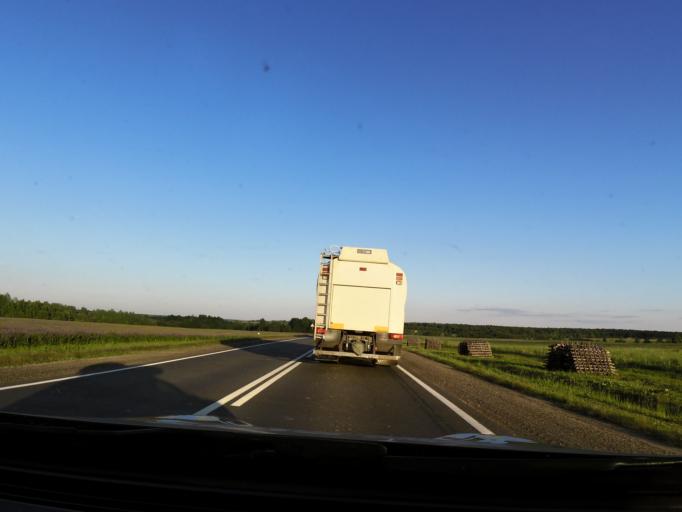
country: RU
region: Vologda
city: Gryazovets
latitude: 58.8286
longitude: 40.2171
